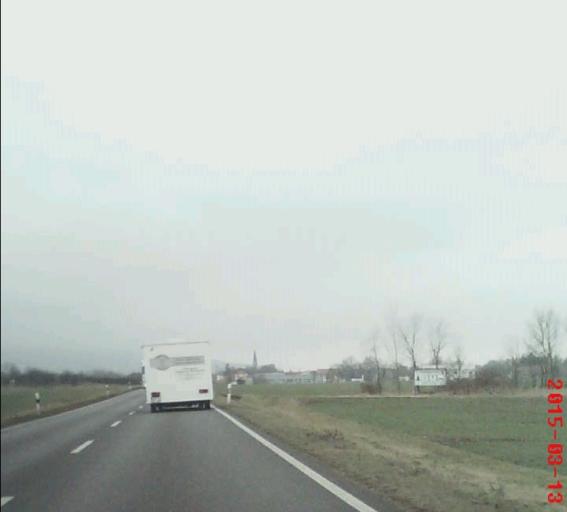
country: DE
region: Thuringia
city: Dachwig
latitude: 51.0786
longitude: 10.8756
